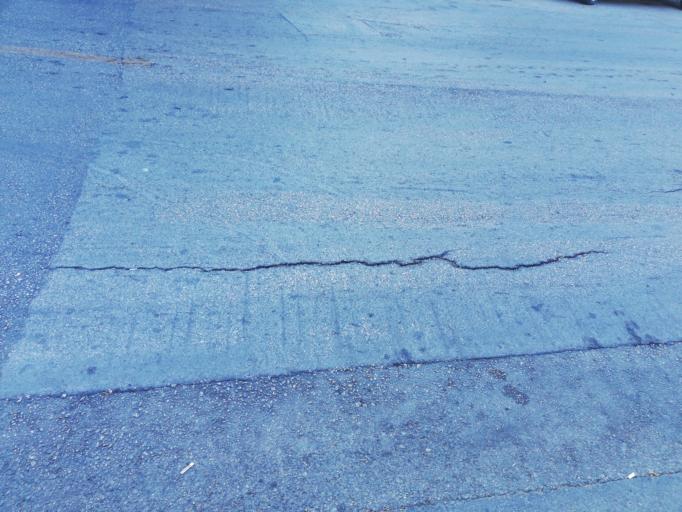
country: LB
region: Mont-Liban
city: Jdaidet el Matn
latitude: 33.9025
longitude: 35.5879
